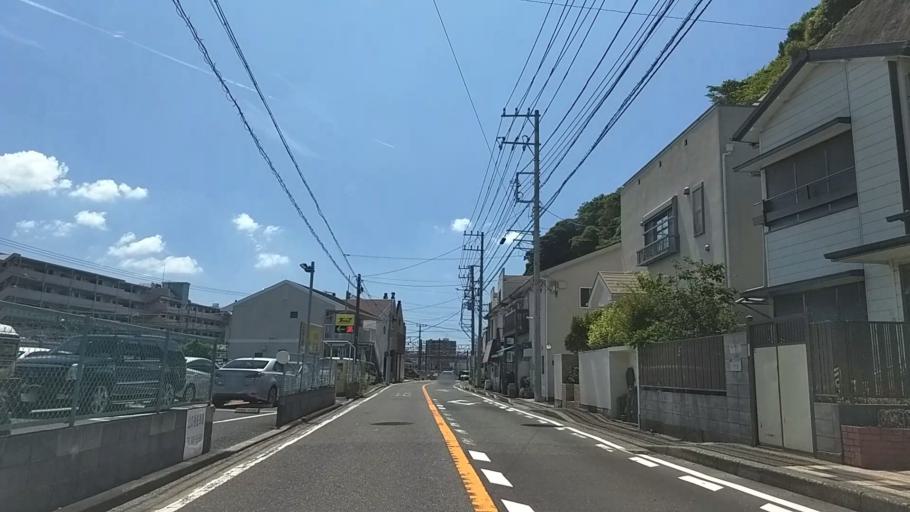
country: JP
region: Kanagawa
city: Zushi
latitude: 35.2995
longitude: 139.5870
